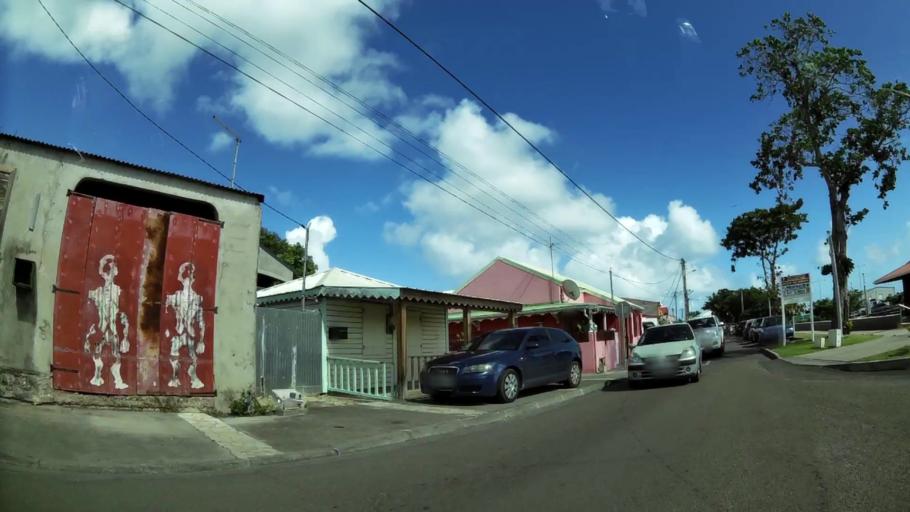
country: GP
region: Guadeloupe
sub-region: Guadeloupe
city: Saint-Francois
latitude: 16.2507
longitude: -61.2712
